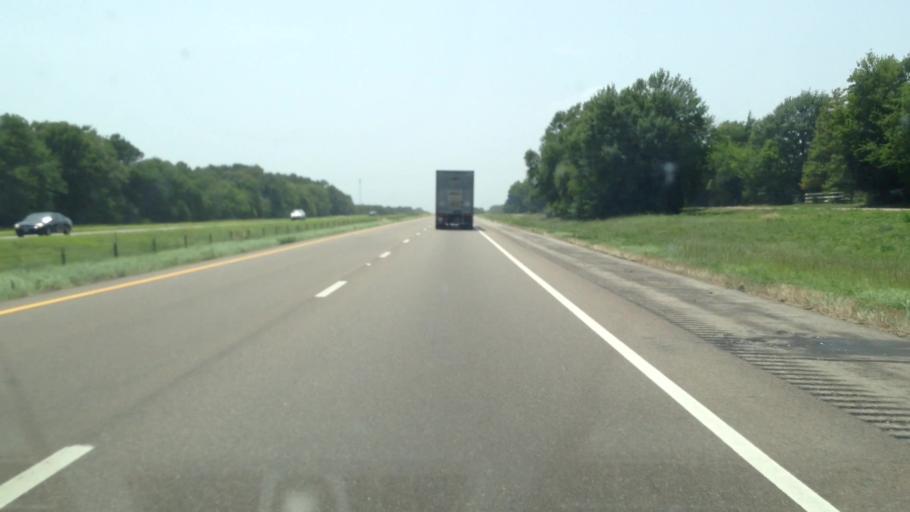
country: US
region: Texas
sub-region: Titus County
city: Mount Pleasant
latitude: 33.1596
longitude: -95.0818
